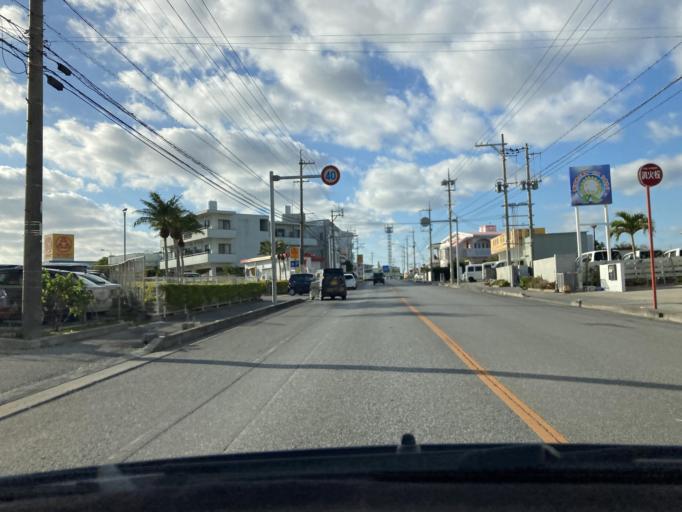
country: JP
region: Okinawa
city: Katsuren-haebaru
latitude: 26.3446
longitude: 127.8739
